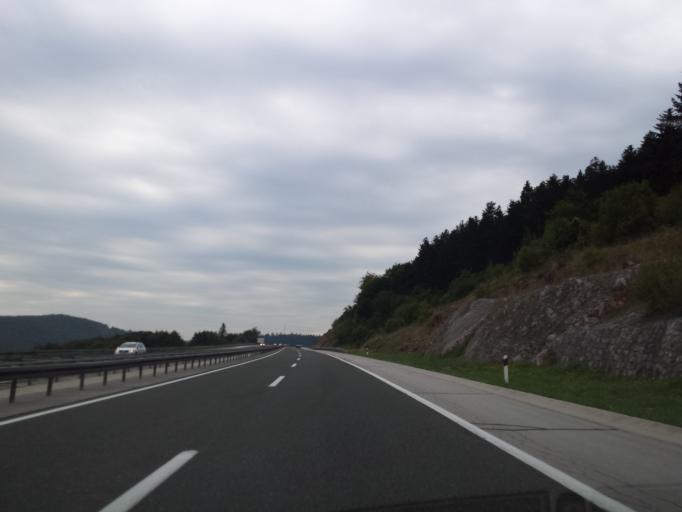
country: HR
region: Licko-Senjska
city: Otocac
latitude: 44.8589
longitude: 15.2153
